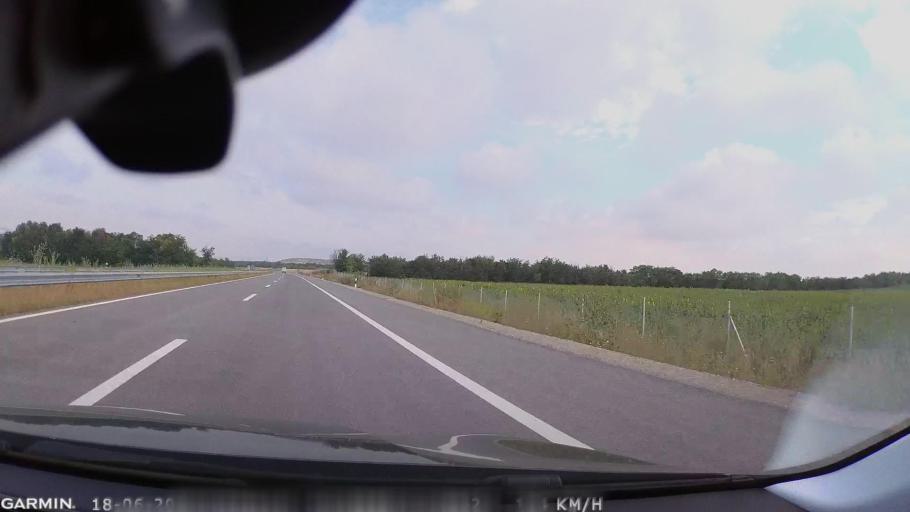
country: MK
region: Sveti Nikole
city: Sveti Nikole
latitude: 41.8390
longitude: 21.9837
